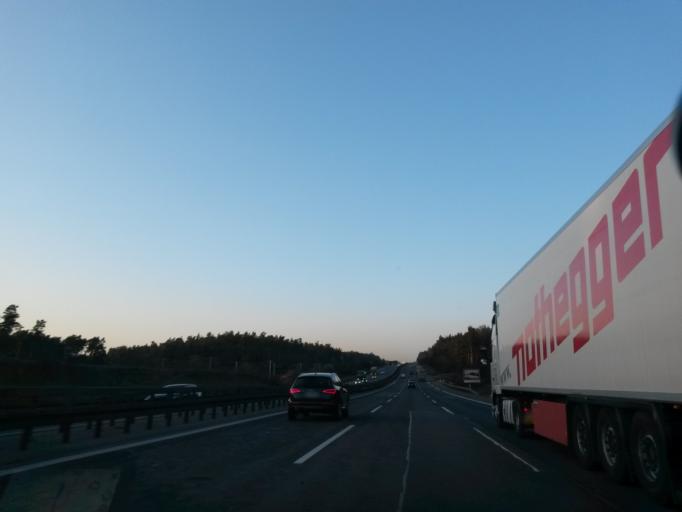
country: DE
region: Bavaria
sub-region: Regierungsbezirk Mittelfranken
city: Allersberg
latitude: 49.2906
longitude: 11.2087
